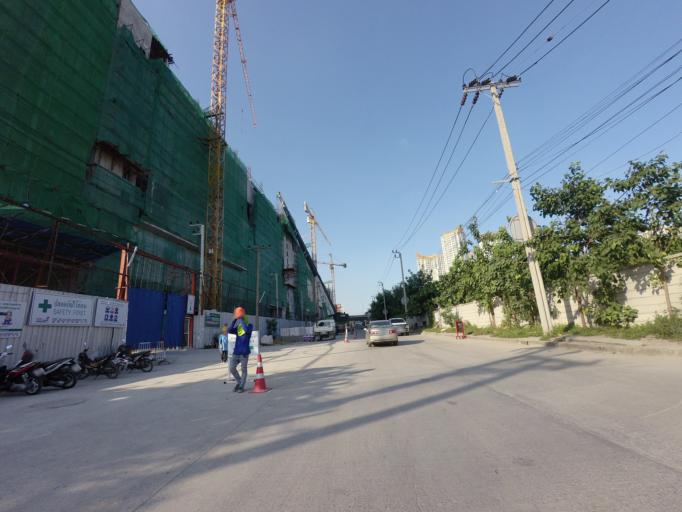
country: TH
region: Bangkok
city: Watthana
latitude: 13.7502
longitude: 100.5728
